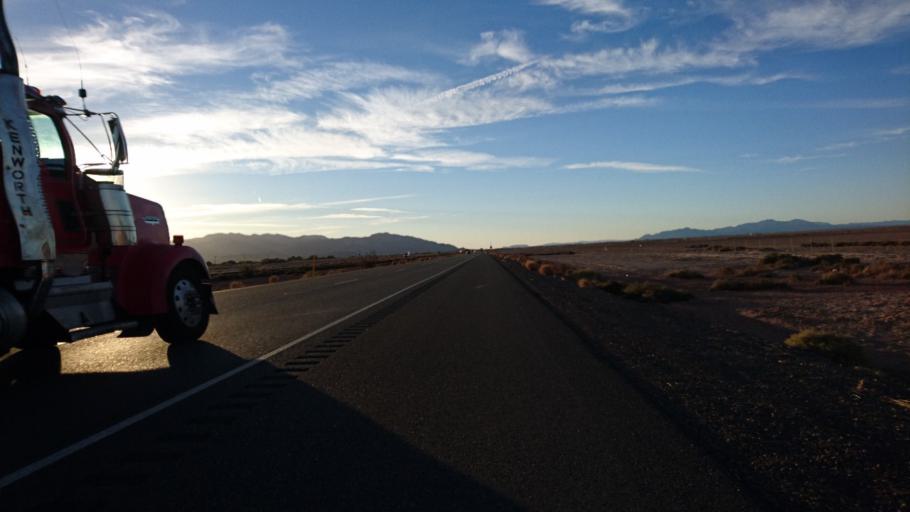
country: US
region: California
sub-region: San Bernardino County
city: Fort Irwin
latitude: 34.8040
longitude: -116.5405
